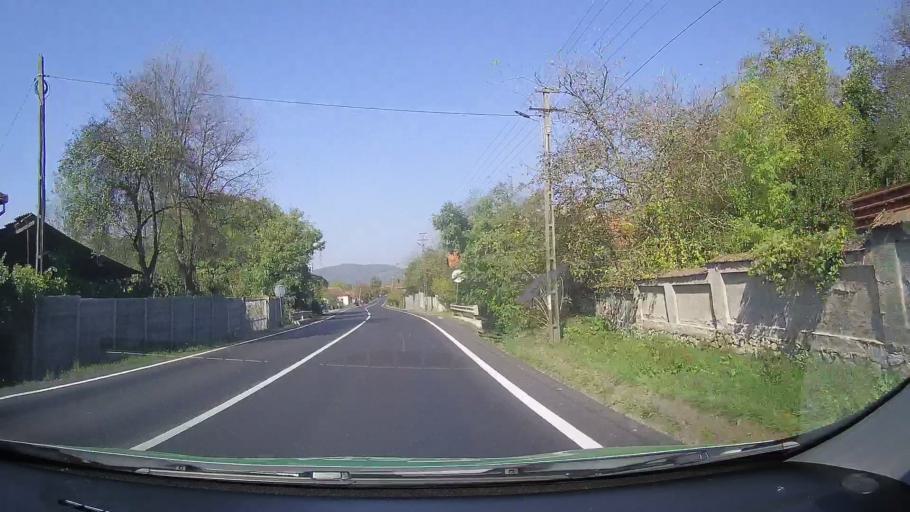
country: RO
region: Hunedoara
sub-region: Comuna Burjuc
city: Burjuc
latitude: 45.9485
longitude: 22.4914
